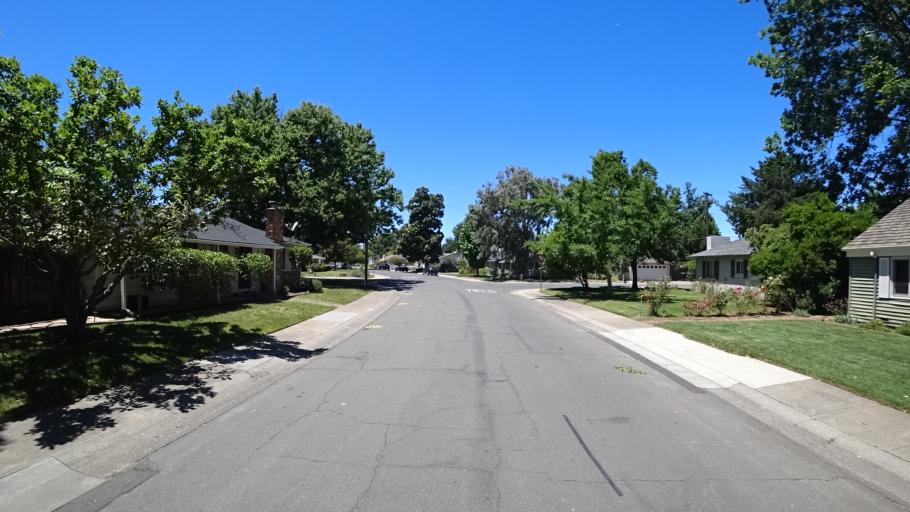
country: US
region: California
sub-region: Sacramento County
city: Sacramento
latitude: 38.5780
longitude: -121.4448
